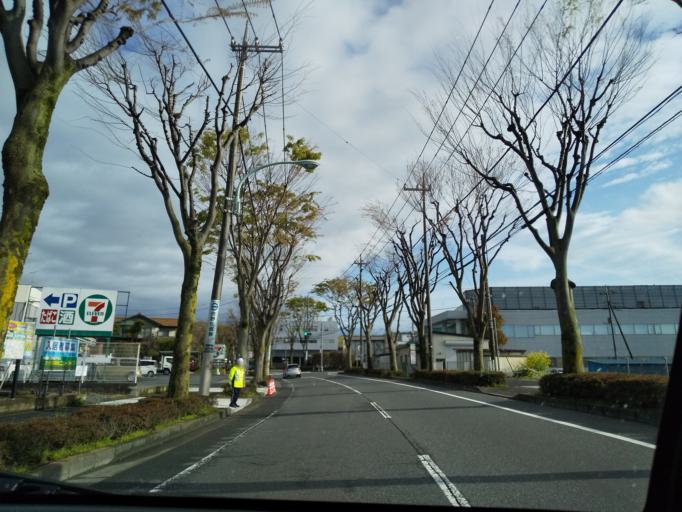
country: JP
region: Tokyo
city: Itsukaichi
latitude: 35.6769
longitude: 139.2572
